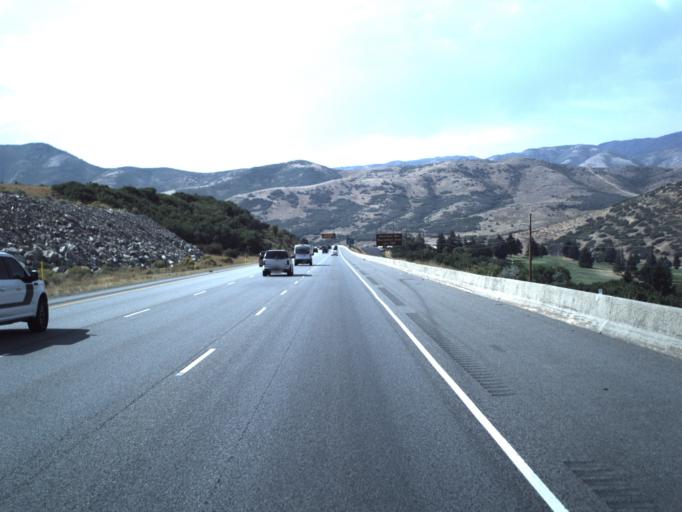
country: US
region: Utah
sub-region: Summit County
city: Summit Park
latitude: 40.7463
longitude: -111.6935
